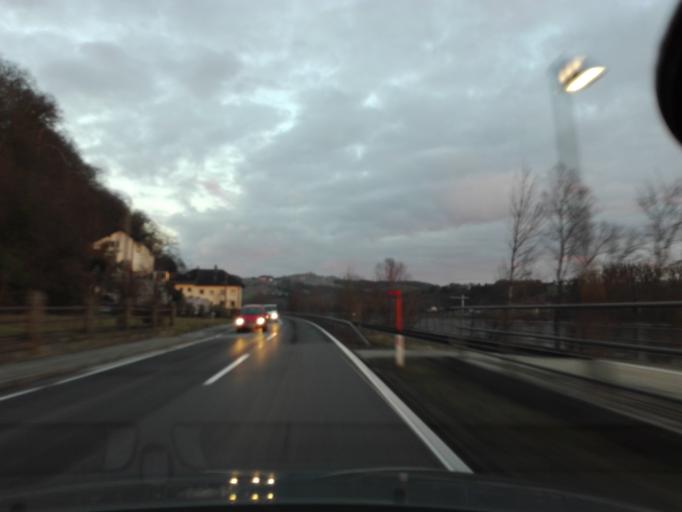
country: AT
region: Upper Austria
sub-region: Politischer Bezirk Perg
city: Bad Kreuzen
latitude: 48.1917
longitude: 14.8212
